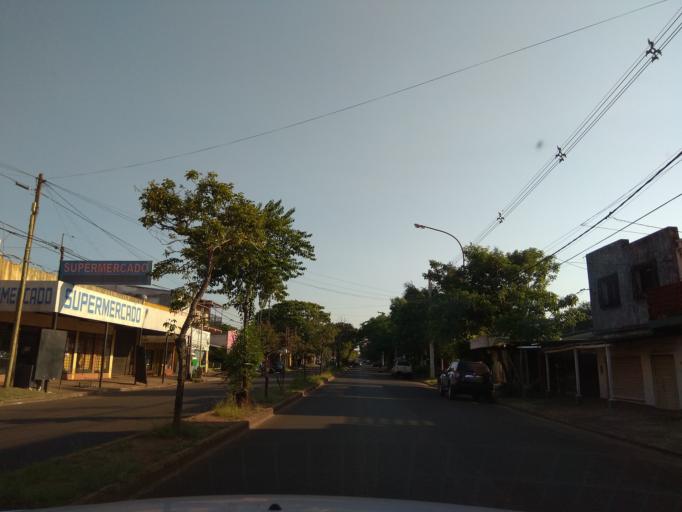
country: AR
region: Misiones
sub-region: Departamento de Capital
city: Posadas
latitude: -27.3743
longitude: -55.9176
